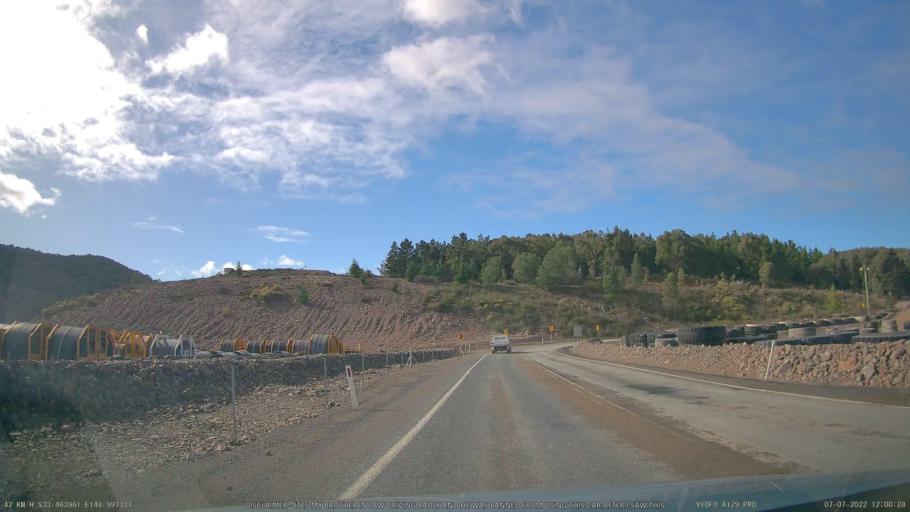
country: AU
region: New South Wales
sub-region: Blayney
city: Millthorpe
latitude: -33.4640
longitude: 148.9977
